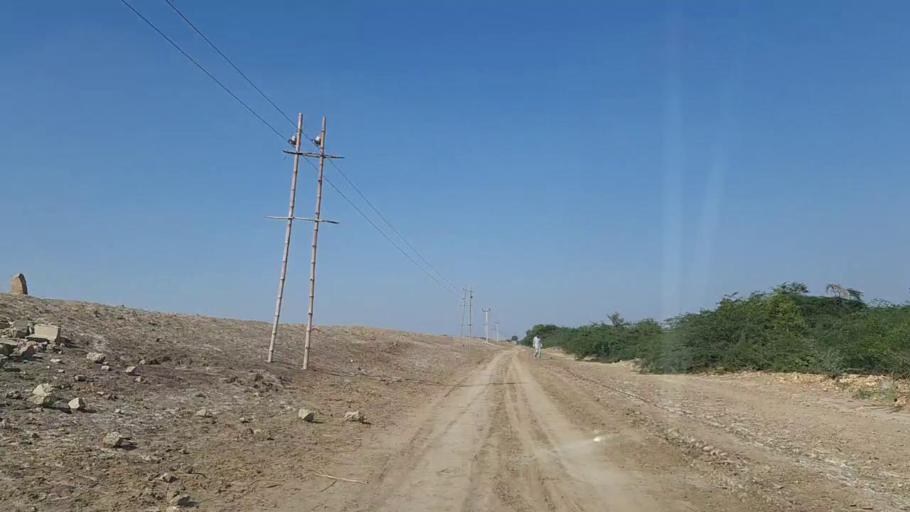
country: PK
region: Sindh
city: Chuhar Jamali
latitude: 24.5421
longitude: 68.0157
